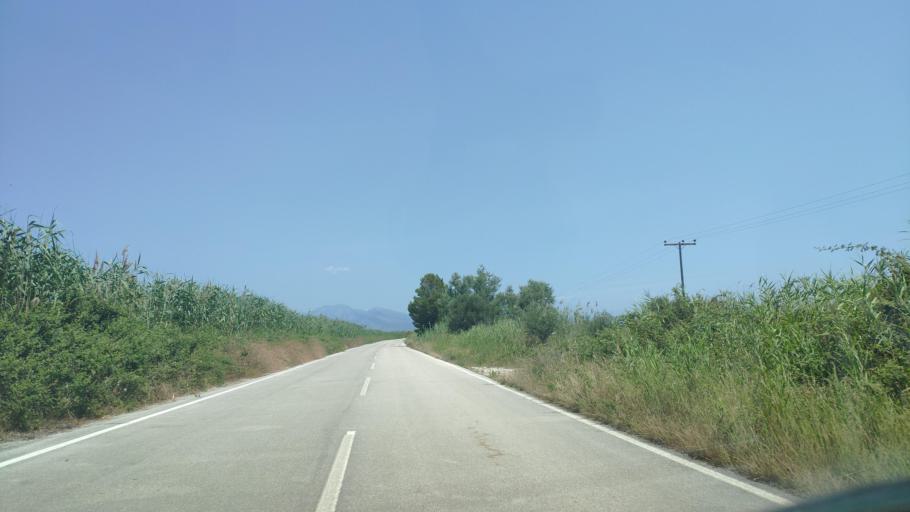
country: GR
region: Epirus
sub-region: Nomos Artas
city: Aneza
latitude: 39.0538
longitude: 20.8640
